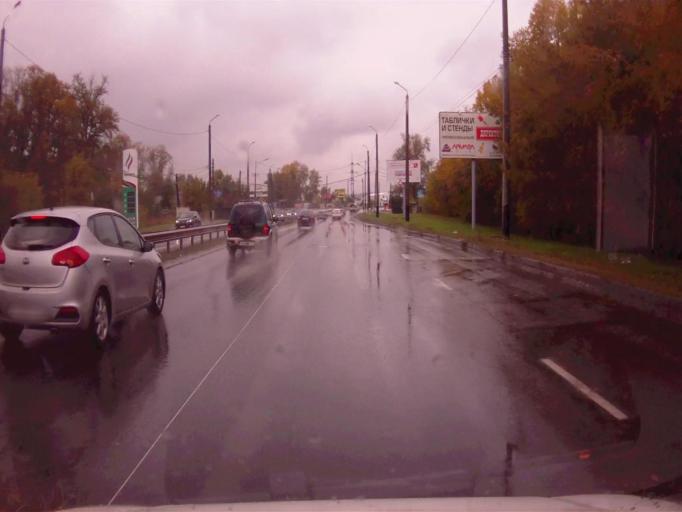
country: RU
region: Chelyabinsk
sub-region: Gorod Chelyabinsk
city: Chelyabinsk
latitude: 55.2358
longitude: 61.3642
